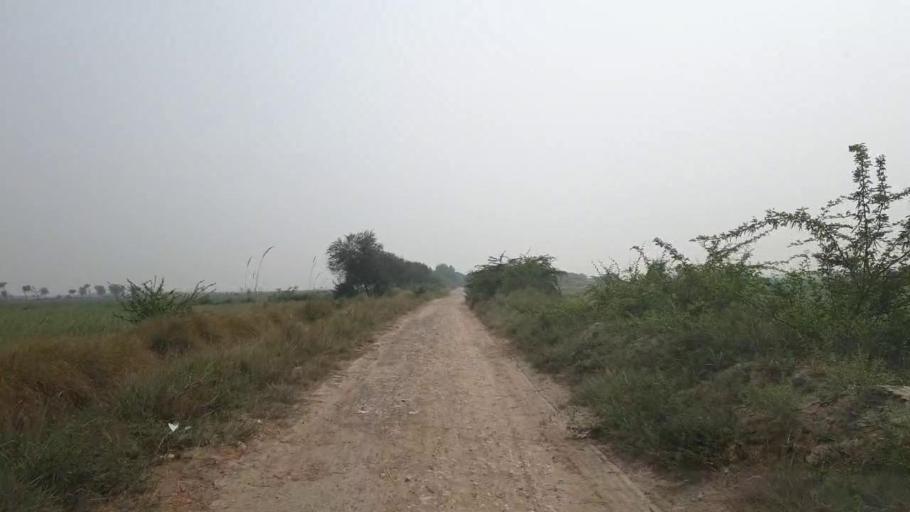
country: PK
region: Sindh
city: Kario
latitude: 24.6527
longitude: 68.6016
